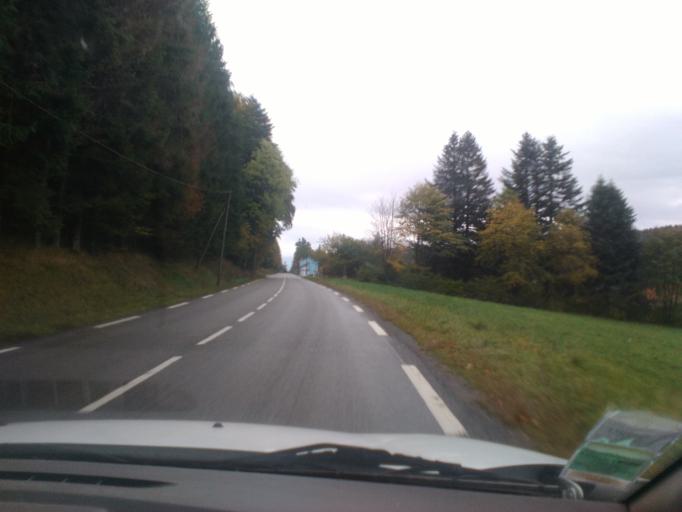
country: FR
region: Lorraine
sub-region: Departement des Vosges
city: Xonrupt-Longemer
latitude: 48.1233
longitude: 6.9131
